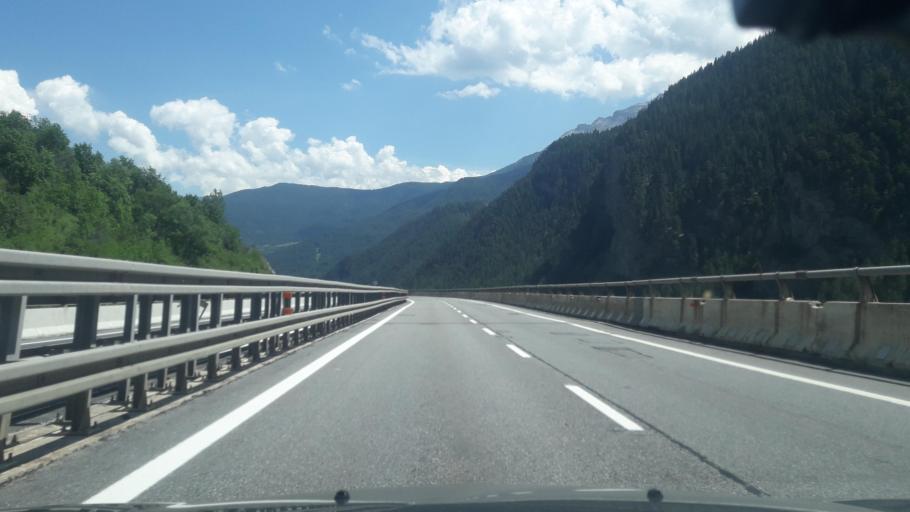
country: IT
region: Piedmont
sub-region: Provincia di Torino
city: Bardonecchia
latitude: 45.0654
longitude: 6.7254
